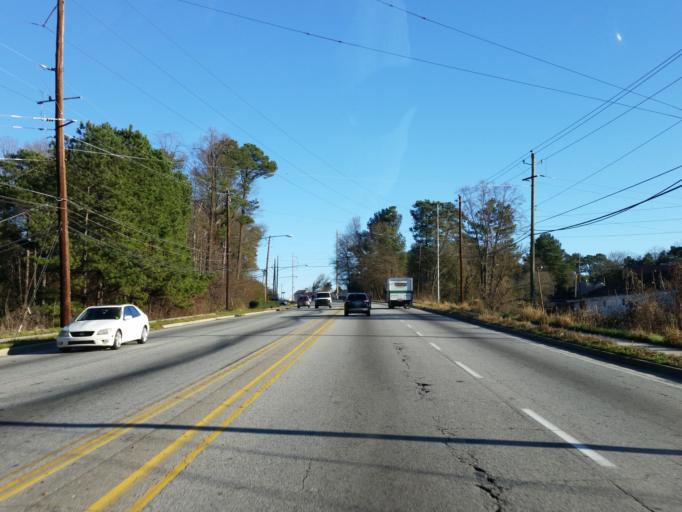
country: US
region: Georgia
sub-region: Cobb County
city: Vinings
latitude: 33.8168
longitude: -84.4469
